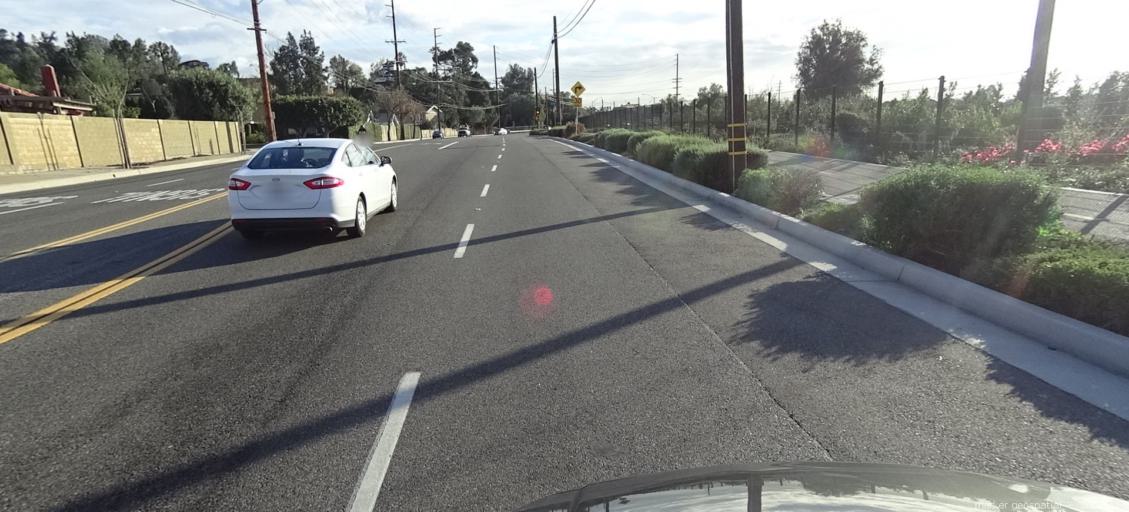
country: US
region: California
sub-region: Orange County
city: Villa Park
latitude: 33.8089
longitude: -117.8010
